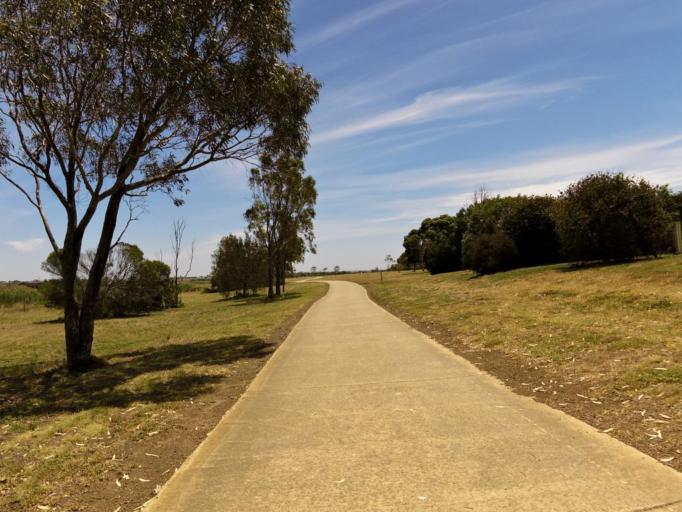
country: AU
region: Victoria
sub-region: Hobsons Bay
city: Altona Meadows
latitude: -37.8932
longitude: 144.7817
